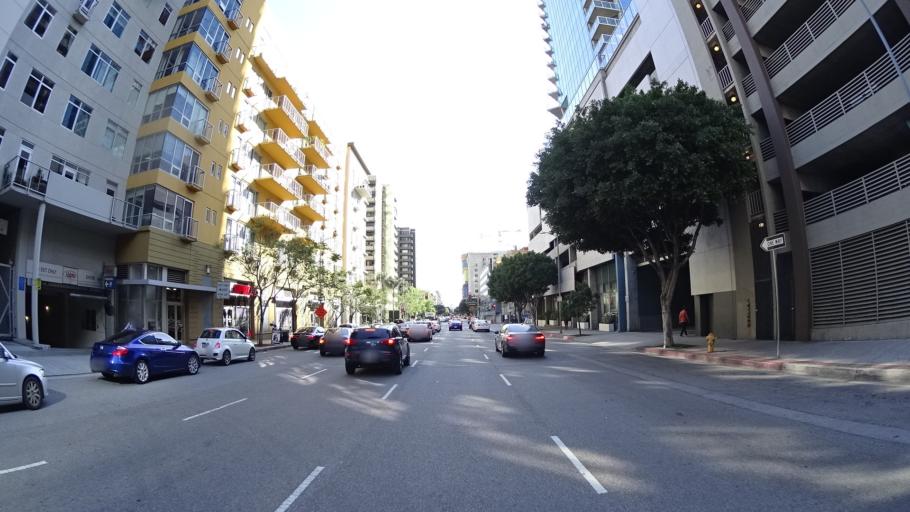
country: US
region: California
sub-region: Los Angeles County
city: Los Angeles
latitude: 34.0466
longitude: -118.2608
